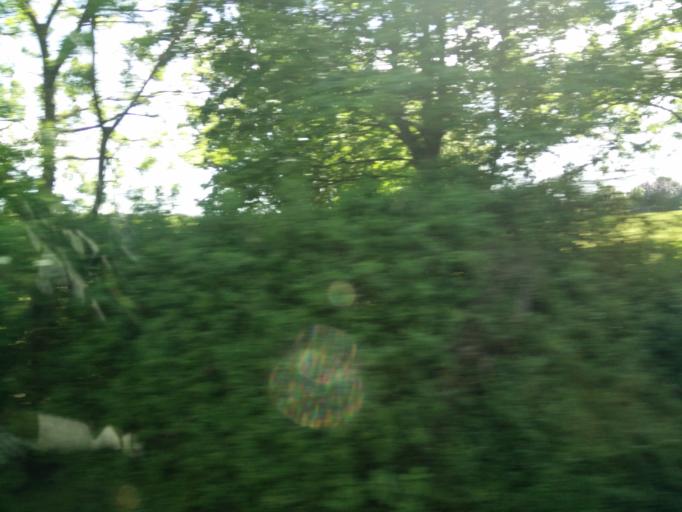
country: GB
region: England
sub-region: Hertfordshire
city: Baldock
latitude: 51.9866
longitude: -0.1949
